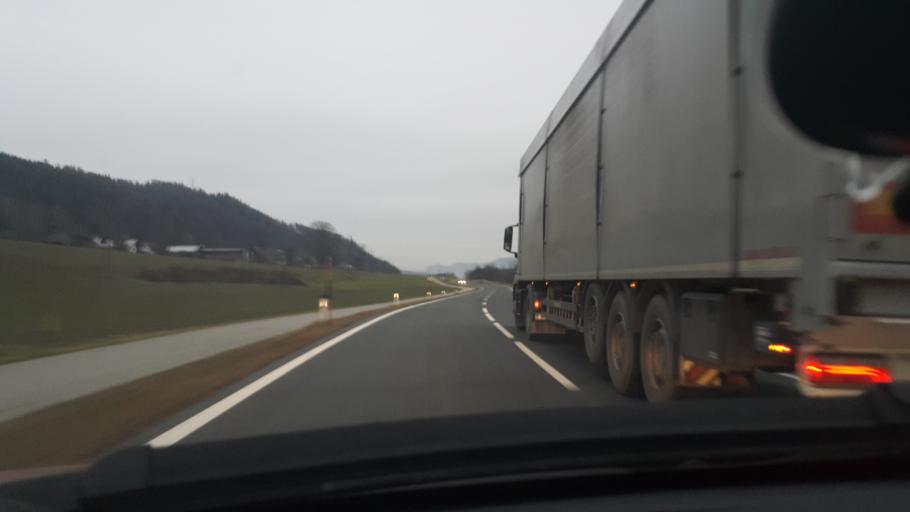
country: AT
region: Carinthia
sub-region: Politischer Bezirk Volkermarkt
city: Ruden
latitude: 46.6484
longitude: 14.7712
